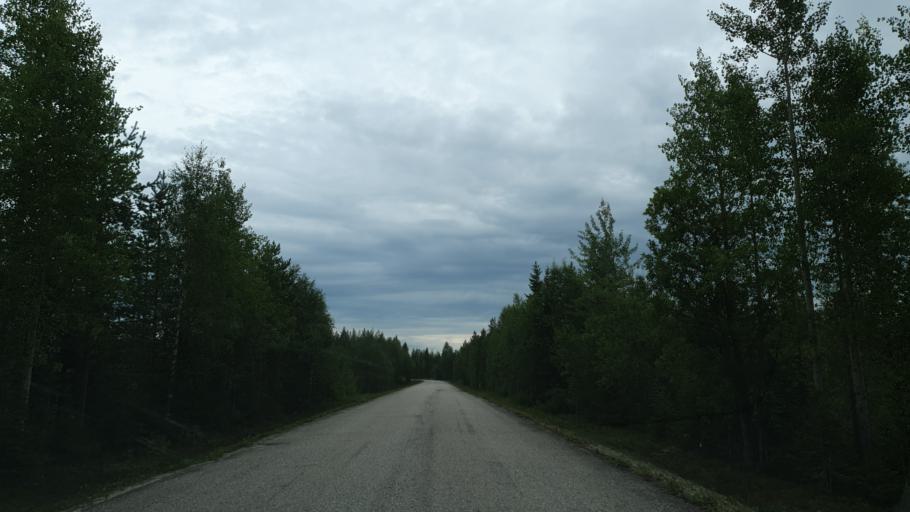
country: FI
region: Kainuu
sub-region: Kehys-Kainuu
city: Kuhmo
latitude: 64.3506
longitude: 29.1295
